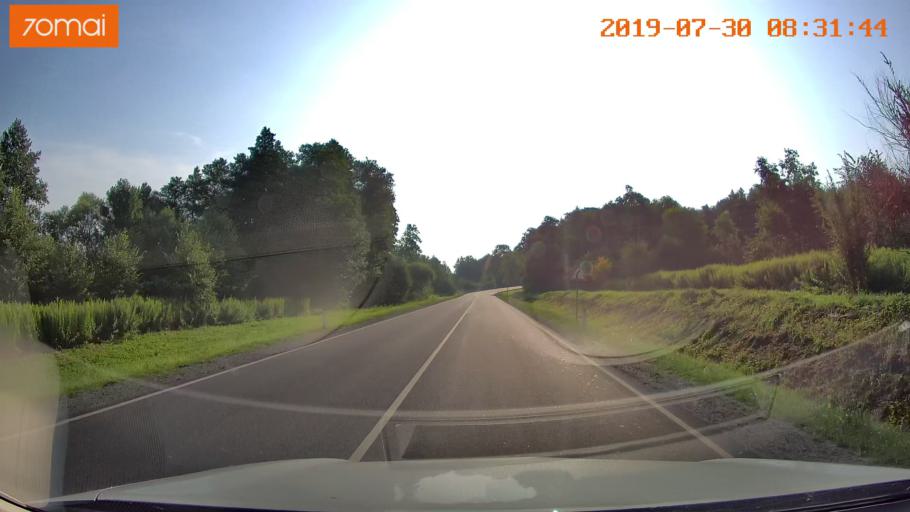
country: RU
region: Kaliningrad
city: Chernyakhovsk
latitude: 54.6387
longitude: 21.7150
